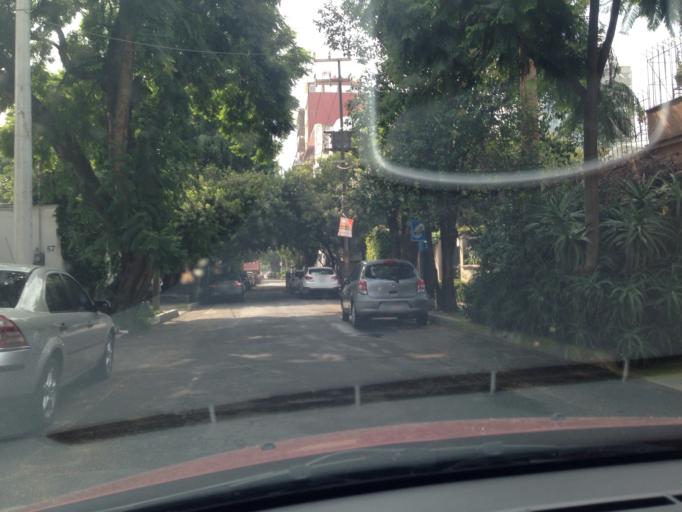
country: MX
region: Mexico City
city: Colonia del Valle
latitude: 19.3723
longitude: -99.1820
